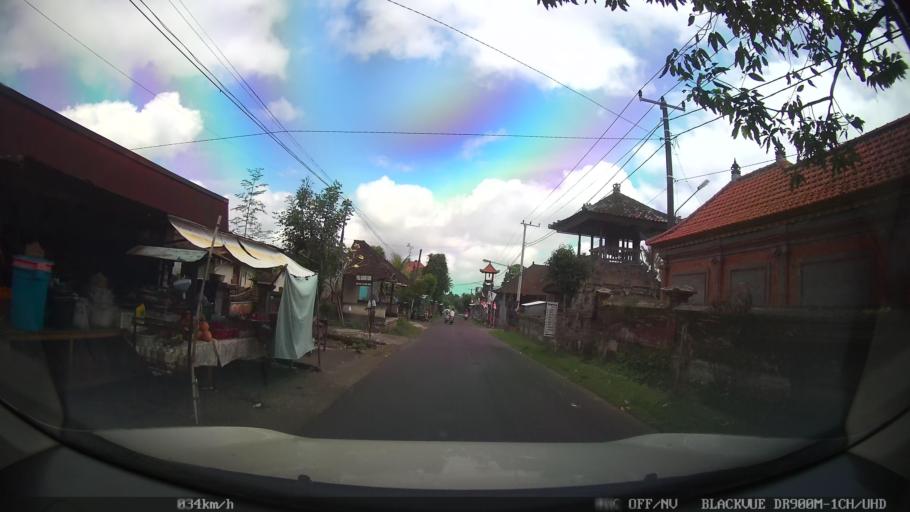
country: ID
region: Bali
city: Banjar Petak
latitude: -8.4504
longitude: 115.3185
